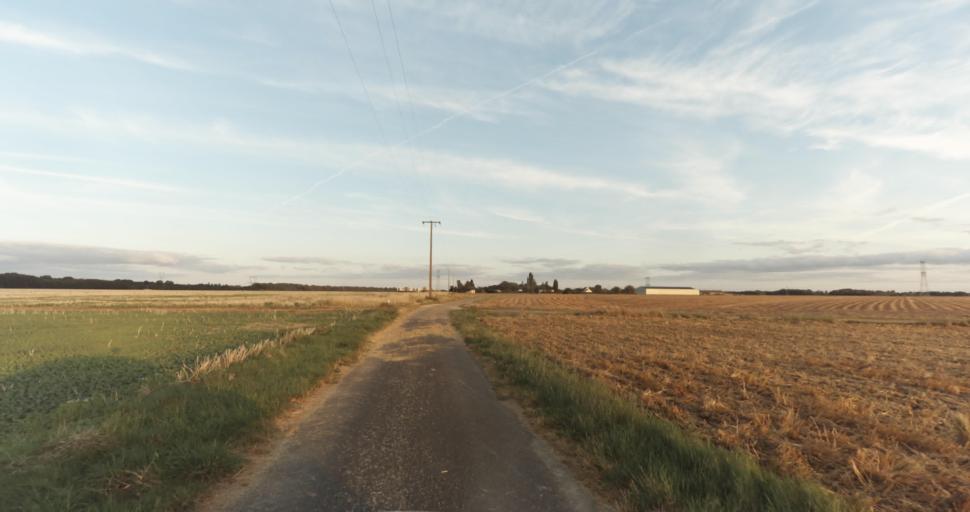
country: FR
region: Haute-Normandie
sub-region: Departement de l'Eure
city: La Madeleine-de-Nonancourt
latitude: 48.8575
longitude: 1.2111
